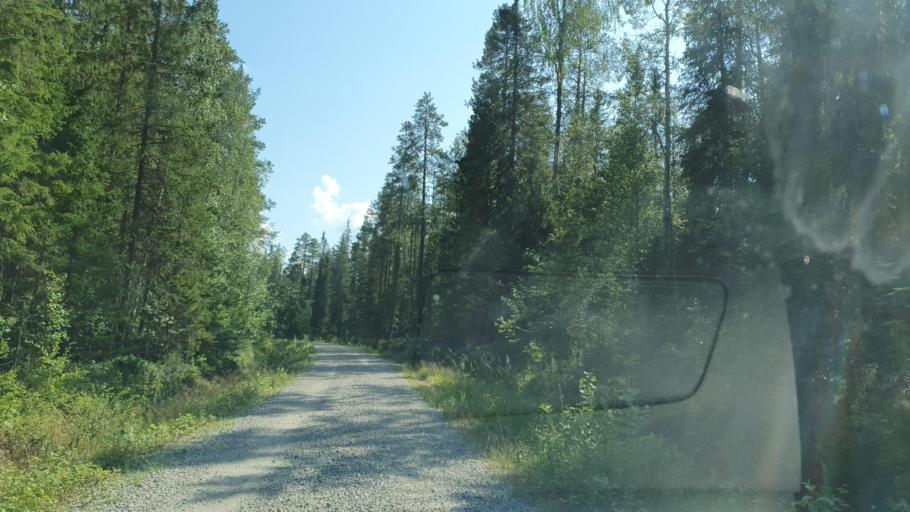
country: FI
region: Kainuu
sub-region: Kehys-Kainuu
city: Kuhmo
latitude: 63.9678
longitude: 29.5393
